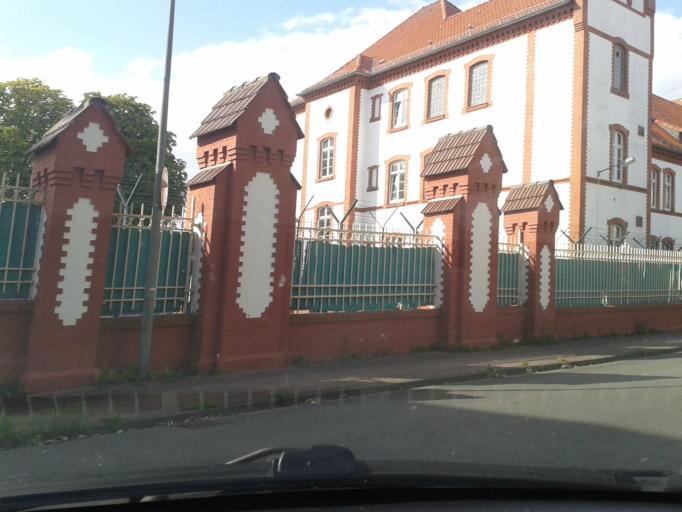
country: DE
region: North Rhine-Westphalia
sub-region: Regierungsbezirk Detmold
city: Paderborn
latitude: 51.7229
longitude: 8.7356
